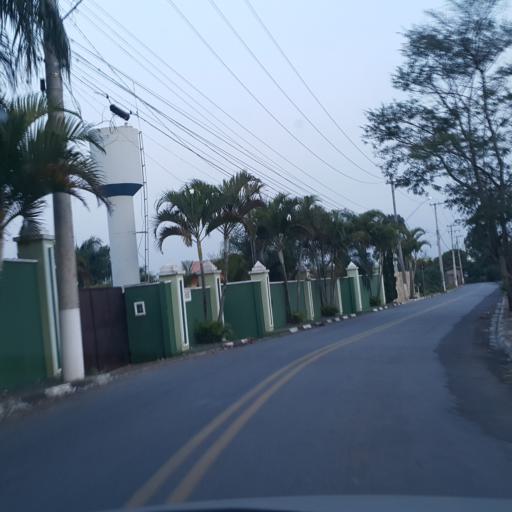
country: BR
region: Sao Paulo
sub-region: Louveira
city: Louveira
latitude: -23.0695
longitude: -46.9574
